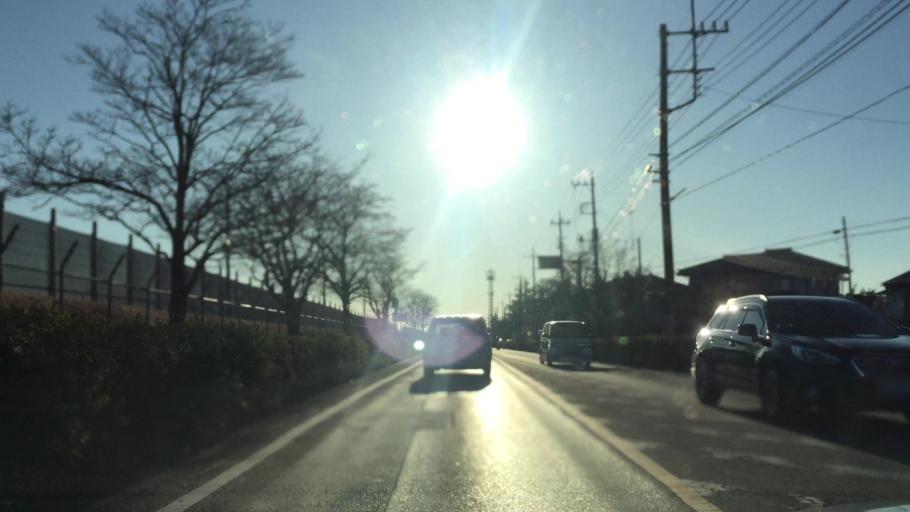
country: JP
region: Gunma
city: Ota
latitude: 36.2697
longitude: 139.3988
